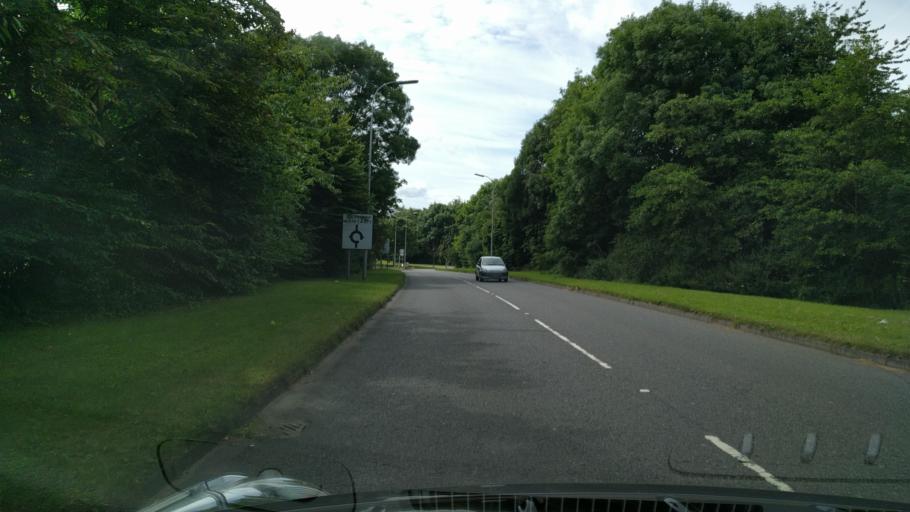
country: GB
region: England
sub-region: Warrington
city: Croft
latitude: 53.4298
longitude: -2.5288
